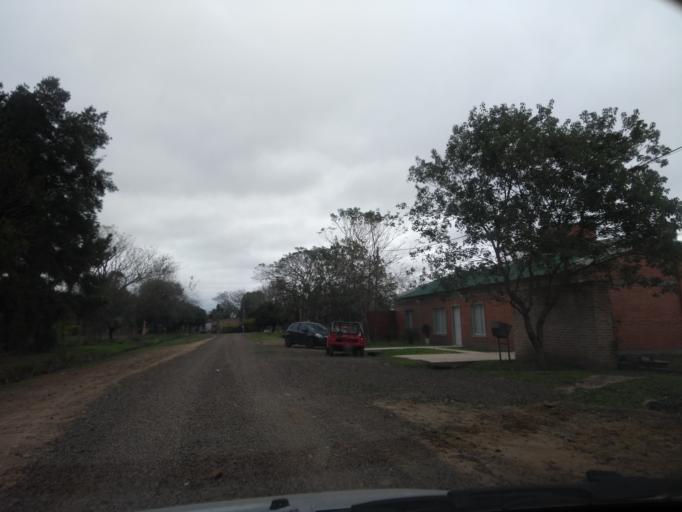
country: AR
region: Chaco
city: Barranqueras
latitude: -27.4251
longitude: -58.9339
